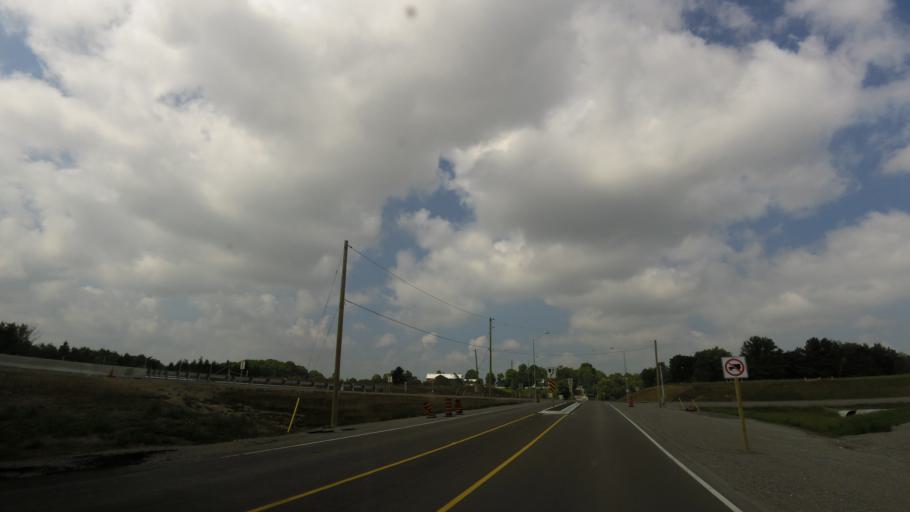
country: CA
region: Ontario
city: Oshawa
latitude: 43.9831
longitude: -78.8689
